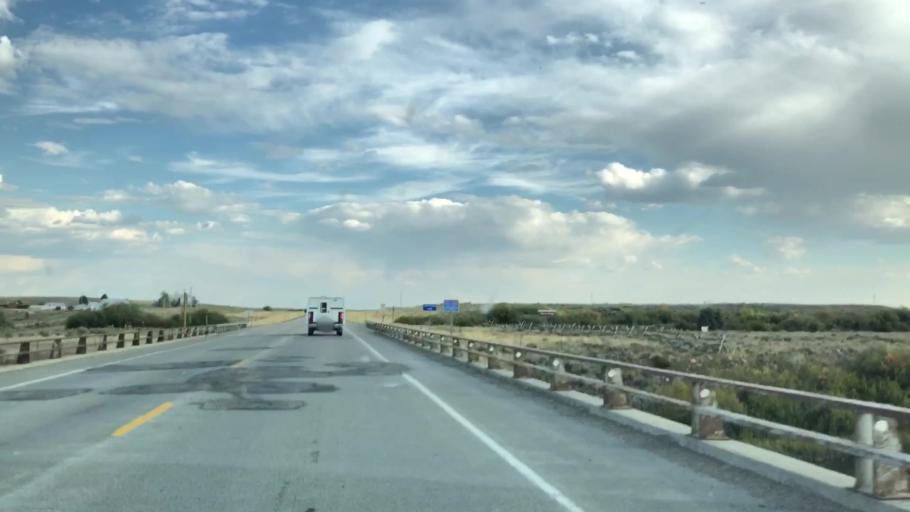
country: US
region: Wyoming
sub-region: Sublette County
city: Pinedale
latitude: 43.0189
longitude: -110.1191
